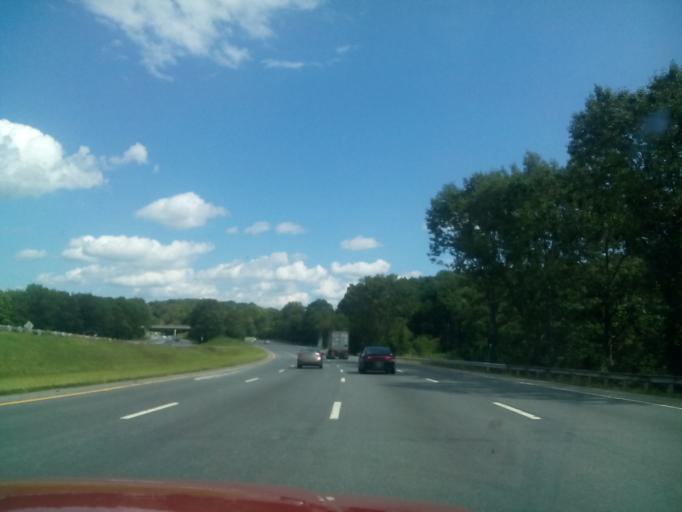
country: US
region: New Jersey
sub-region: Warren County
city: Belvidere
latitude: 40.9228
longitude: -75.0642
